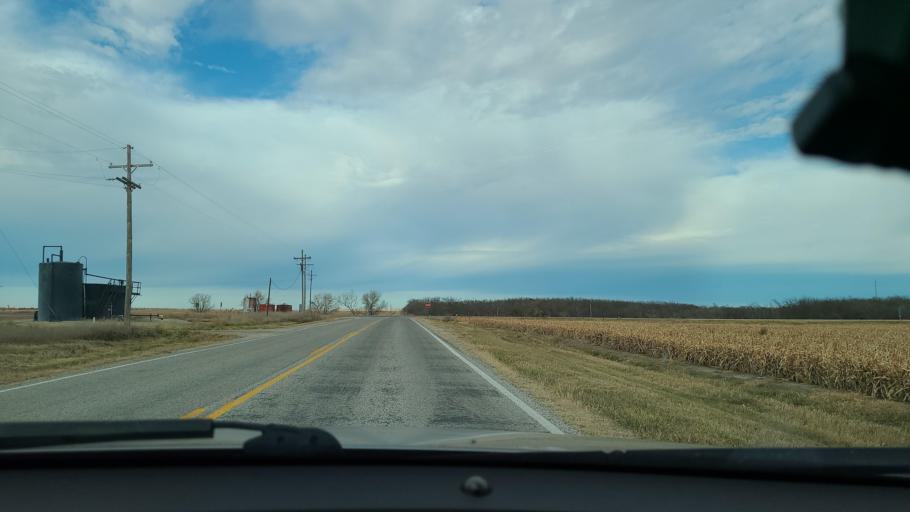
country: US
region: Kansas
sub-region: McPherson County
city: Inman
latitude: 38.3757
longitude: -97.9244
